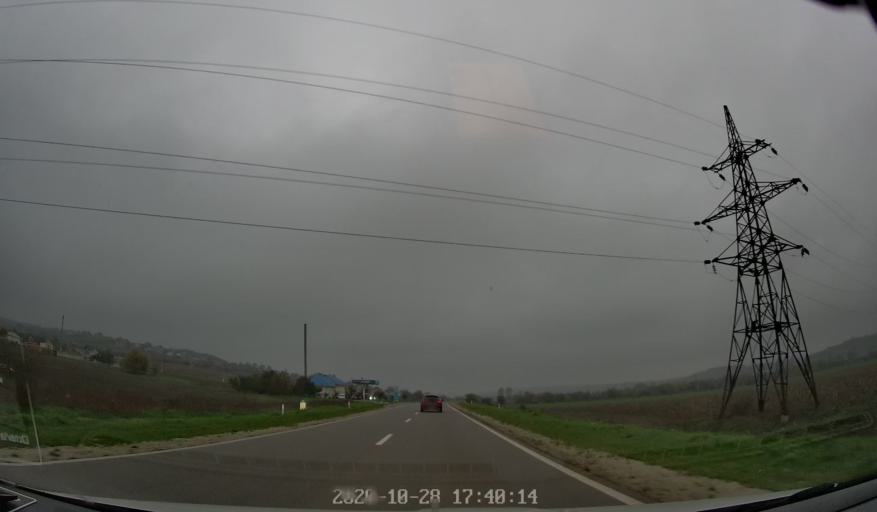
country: MD
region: Hincesti
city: Hincesti
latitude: 46.8082
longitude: 28.6117
